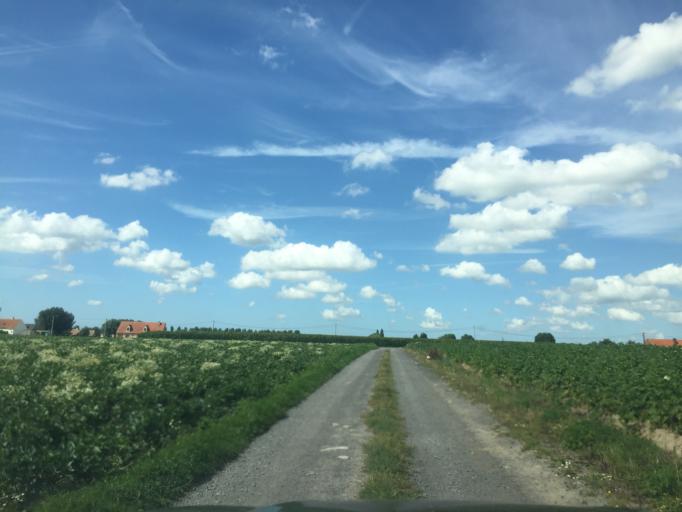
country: BE
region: Flanders
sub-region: Provincie West-Vlaanderen
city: Hooglede
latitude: 50.9978
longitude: 3.0571
